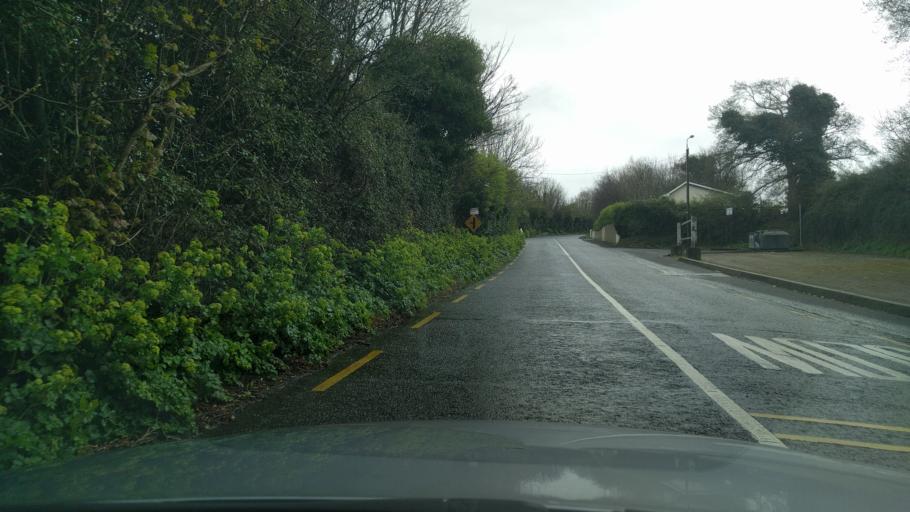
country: IE
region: Leinster
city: Oldbawn
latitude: 53.2640
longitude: -6.3602
